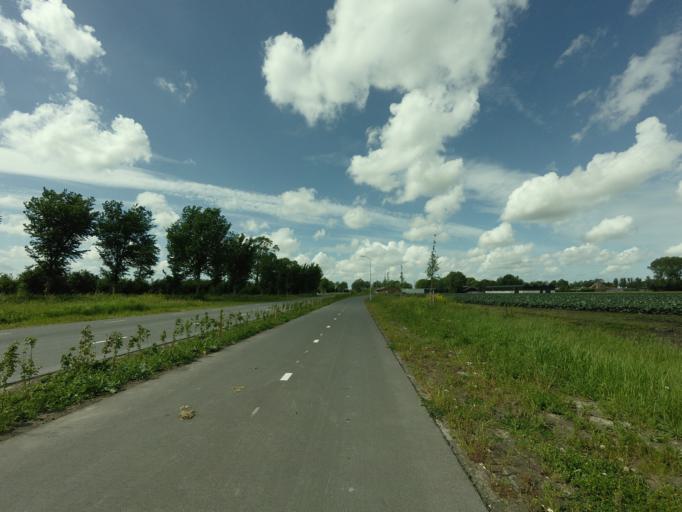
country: NL
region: North Holland
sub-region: Gemeente Hoorn
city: Hoorn
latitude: 52.6835
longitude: 5.0874
